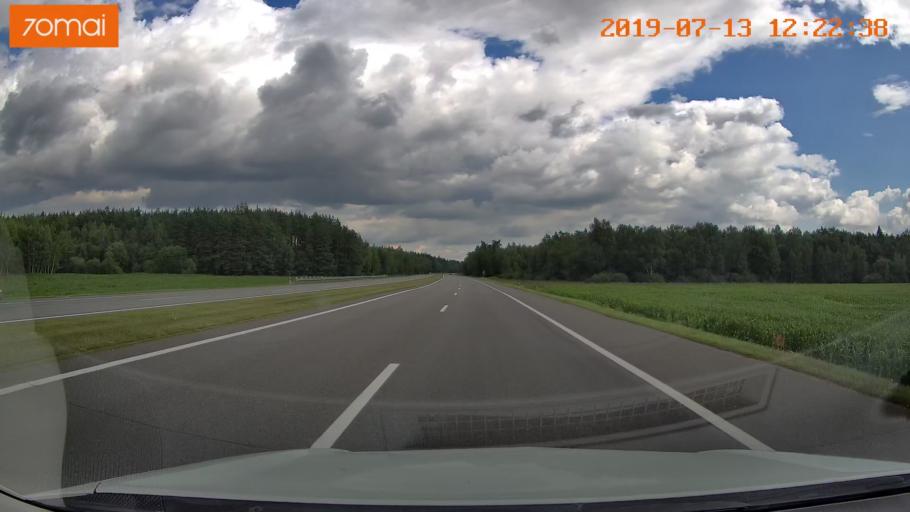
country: BY
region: Minsk
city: Hatava
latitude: 53.7472
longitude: 27.6372
